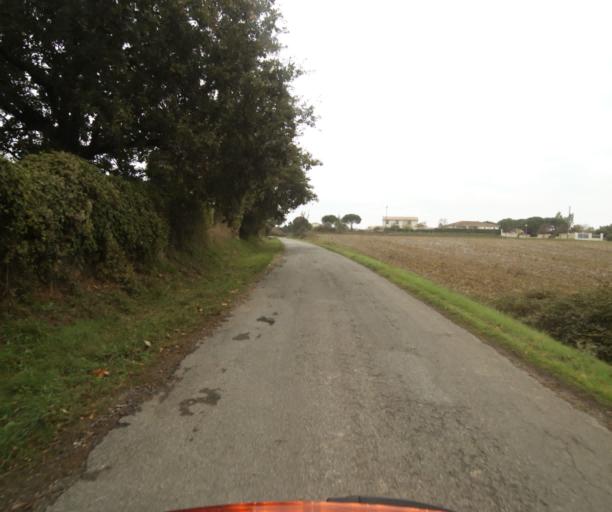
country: FR
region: Midi-Pyrenees
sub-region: Departement du Tarn-et-Garonne
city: Verdun-sur-Garonne
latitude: 43.7982
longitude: 1.2131
